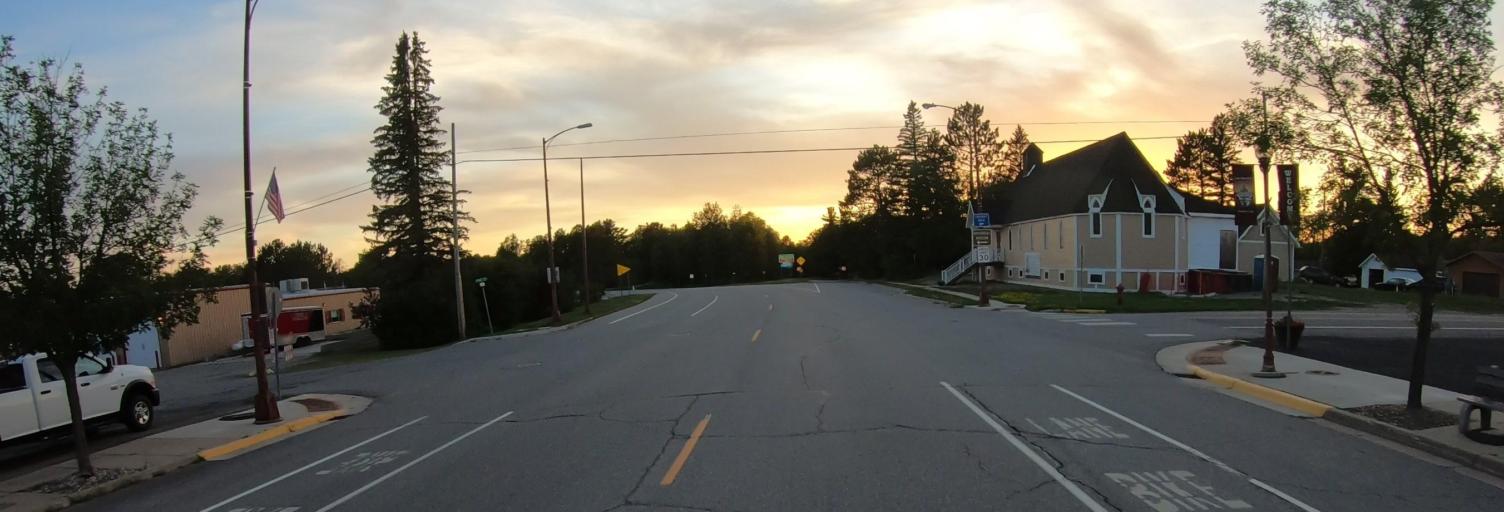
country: US
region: Minnesota
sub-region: Saint Louis County
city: Aurora
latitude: 47.8054
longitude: -92.2782
